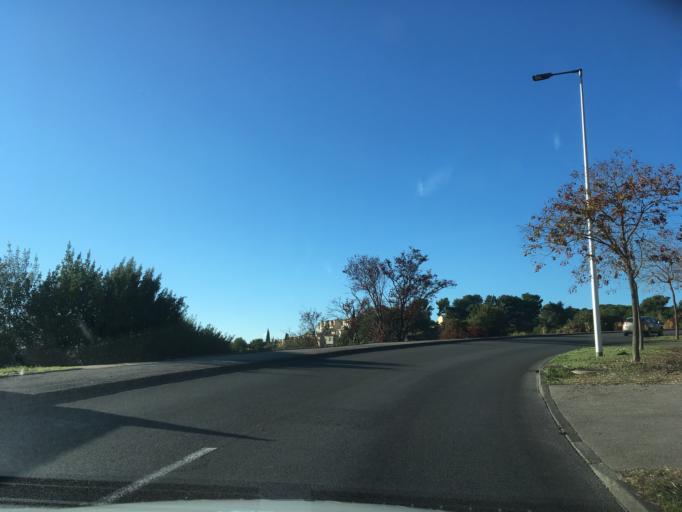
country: FR
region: Languedoc-Roussillon
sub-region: Departement de l'Herault
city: Juvignac
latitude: 43.6345
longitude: 3.8169
